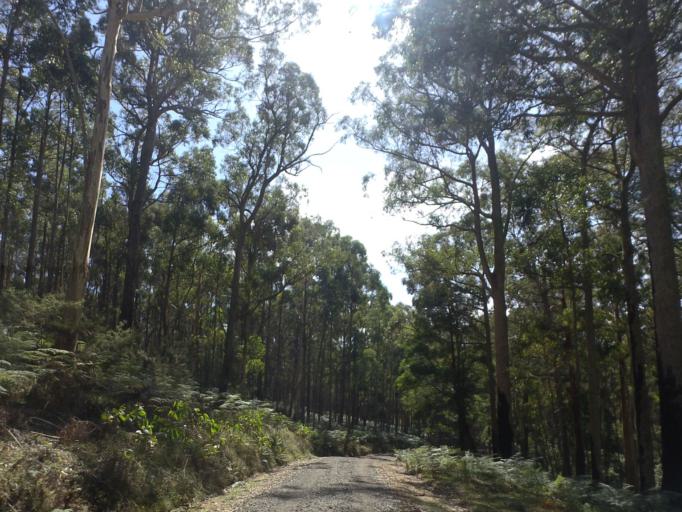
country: AU
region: Victoria
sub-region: Moorabool
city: Bacchus Marsh
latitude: -37.4204
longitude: 144.3386
